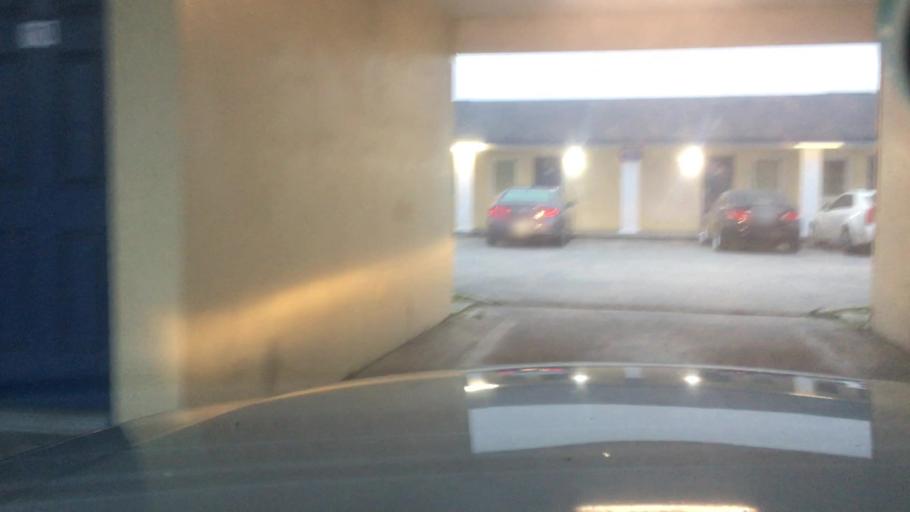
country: US
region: North Carolina
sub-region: Cumberland County
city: Fayetteville
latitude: 35.0109
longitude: -78.8963
